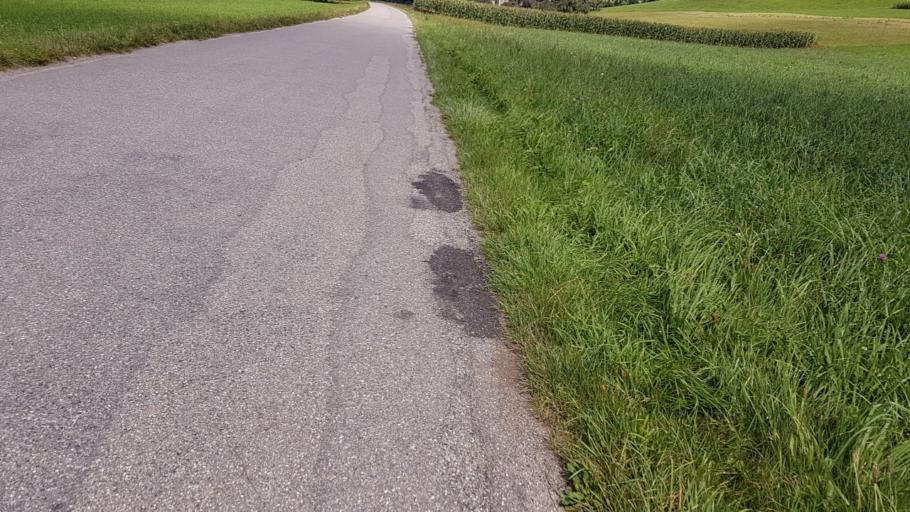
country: CH
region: Lucerne
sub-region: Entlebuch District
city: Oberdiessbach
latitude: 46.8532
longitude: 7.6233
